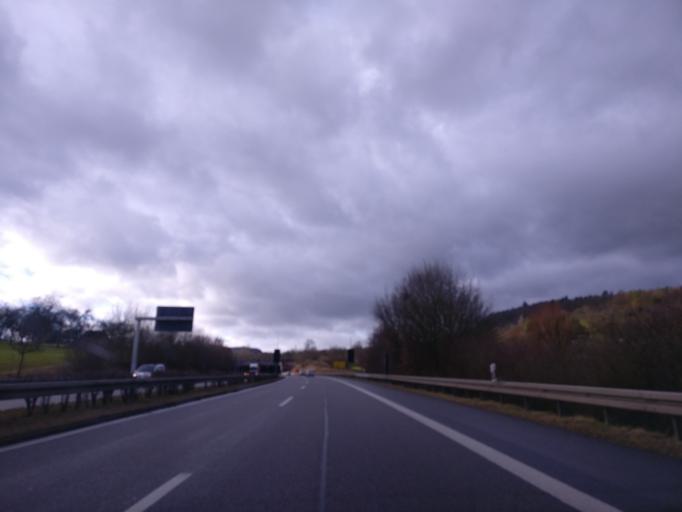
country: DE
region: Baden-Wuerttemberg
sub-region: Regierungsbezirk Stuttgart
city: Schorndorf
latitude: 48.8216
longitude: 9.5376
